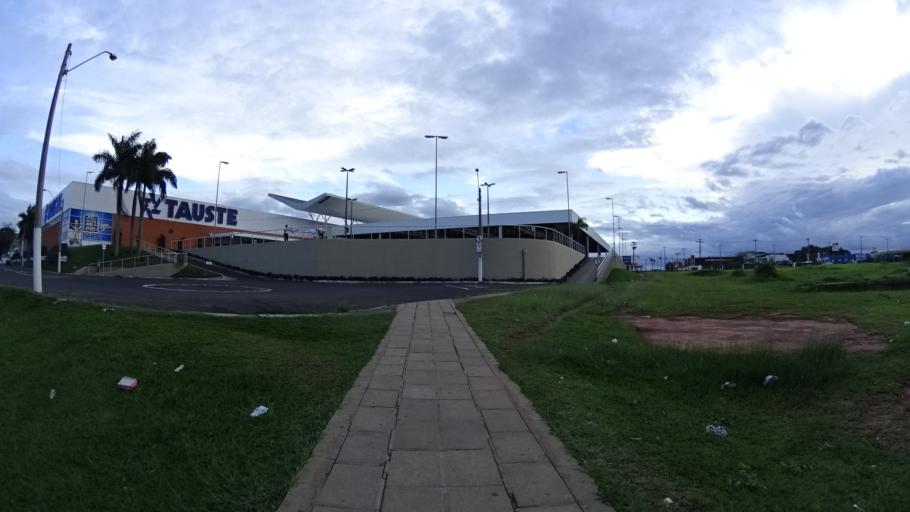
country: BR
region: Sao Paulo
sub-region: Marilia
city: Marilia
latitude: -22.2249
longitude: -49.9333
